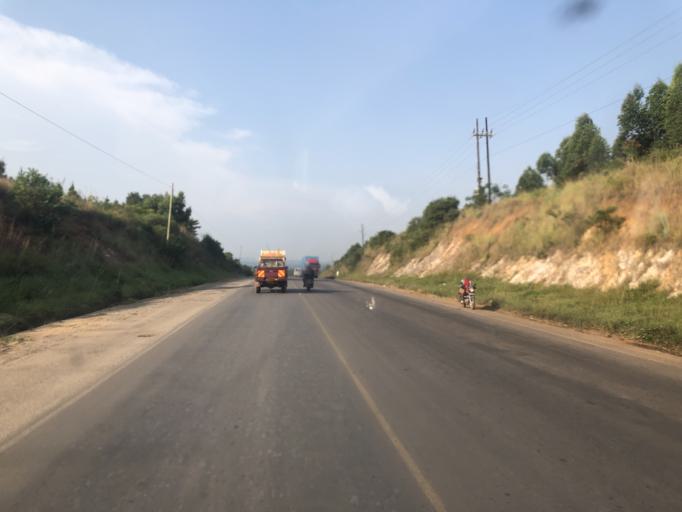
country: UG
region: Central Region
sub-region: Butambala District
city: Gombe
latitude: 0.0764
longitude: 32.1240
